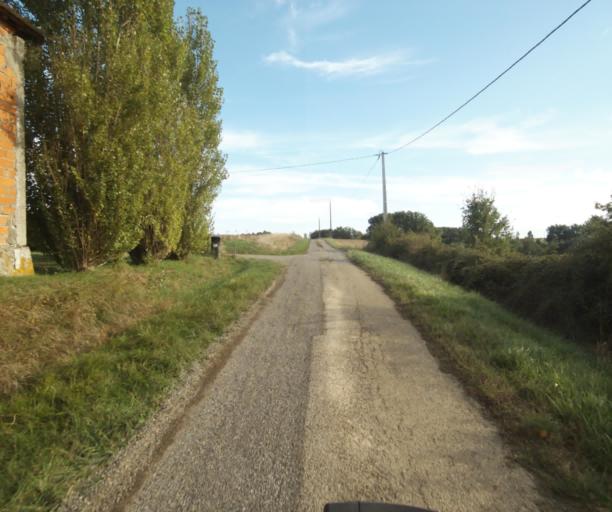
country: FR
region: Midi-Pyrenees
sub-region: Departement du Tarn-et-Garonne
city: Finhan
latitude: 43.9155
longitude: 1.1090
